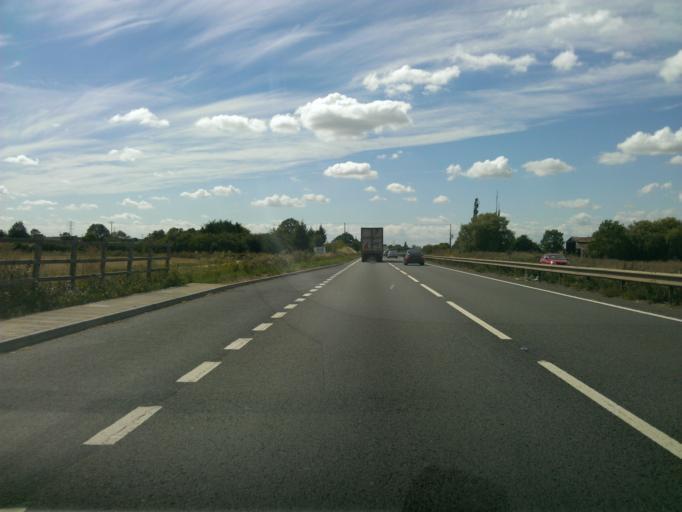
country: GB
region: England
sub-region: Cambridgeshire
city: Buckden
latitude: 52.3322
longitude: -0.2704
